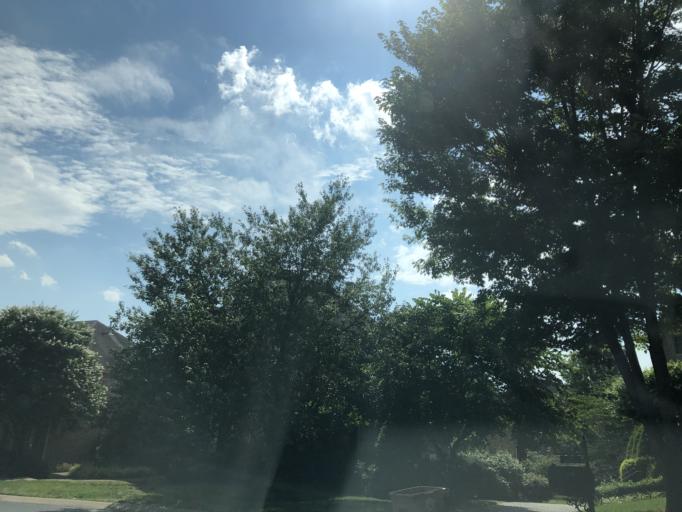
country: US
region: Tennessee
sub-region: Davidson County
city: Belle Meade
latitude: 36.1297
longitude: -86.8237
